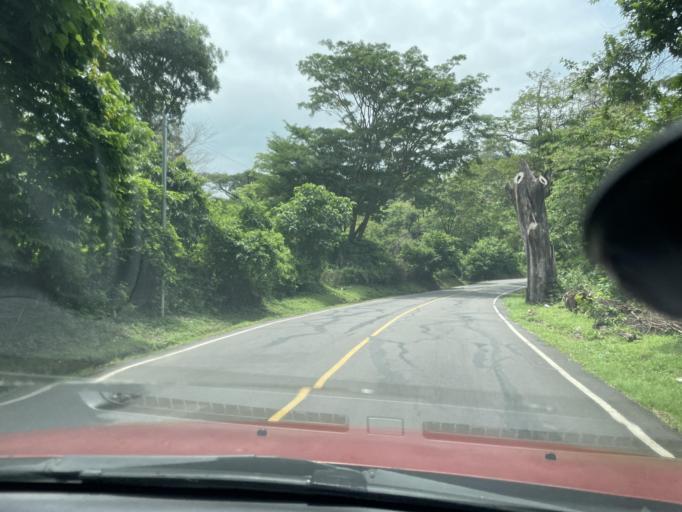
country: SV
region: La Union
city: Santa Rosa de Lima
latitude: 13.6519
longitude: -87.8413
